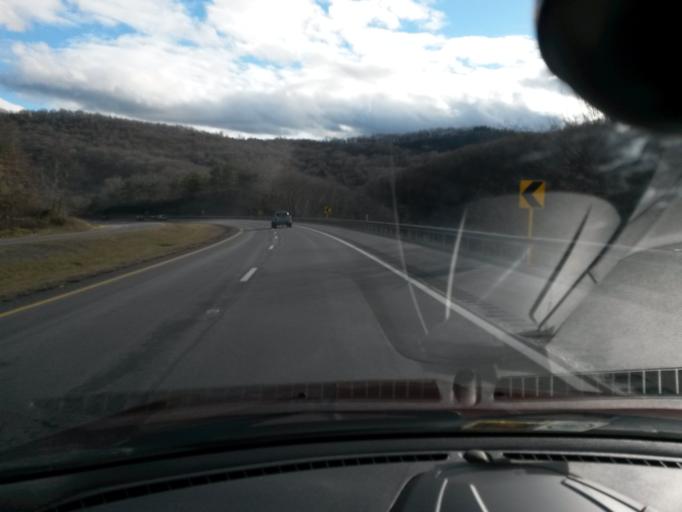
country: US
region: West Virginia
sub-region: Mercer County
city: Athens
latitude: 37.3442
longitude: -81.0136
